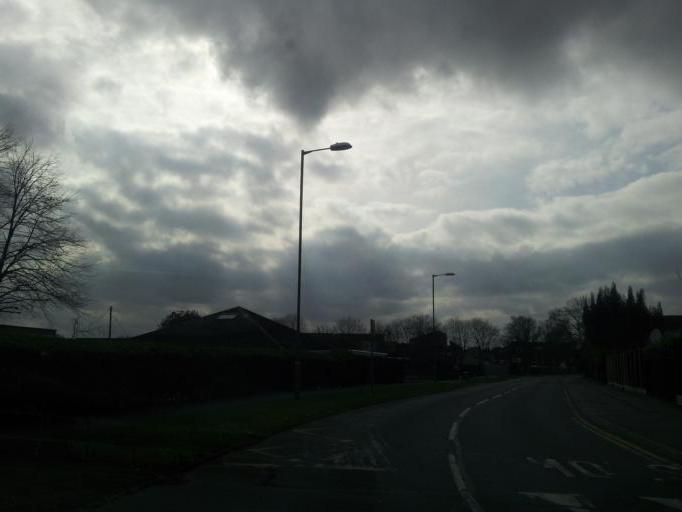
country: GB
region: England
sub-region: Hertfordshire
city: Hoddesdon
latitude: 51.7770
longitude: -0.0053
